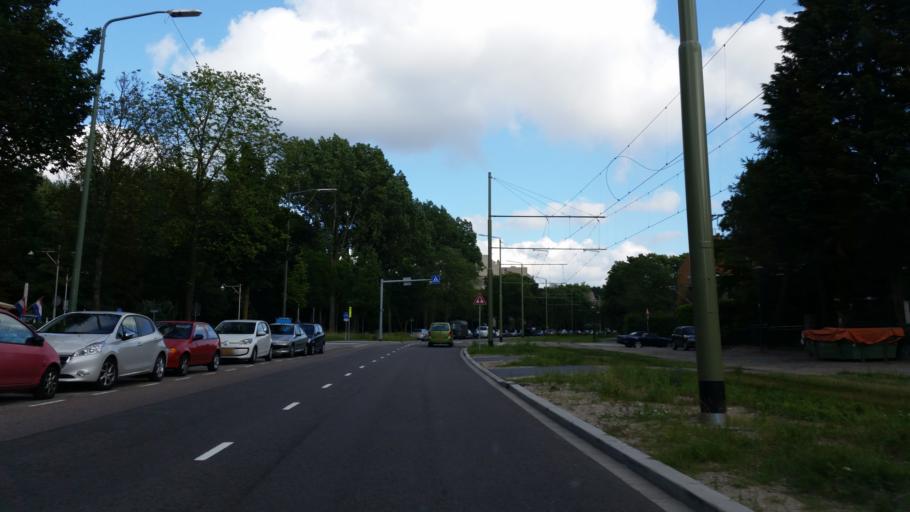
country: NL
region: South Holland
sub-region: Gemeente Den Haag
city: Scheveningen
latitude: 52.1061
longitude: 4.2935
